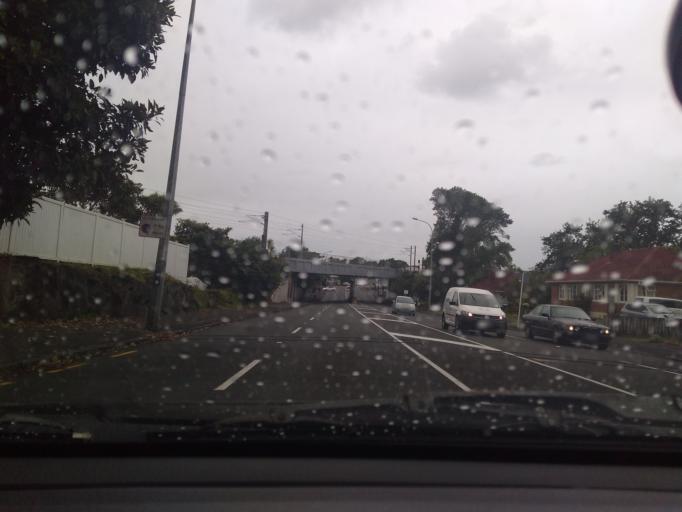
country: NZ
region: Auckland
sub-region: Auckland
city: Auckland
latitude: -36.8768
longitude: 174.7306
